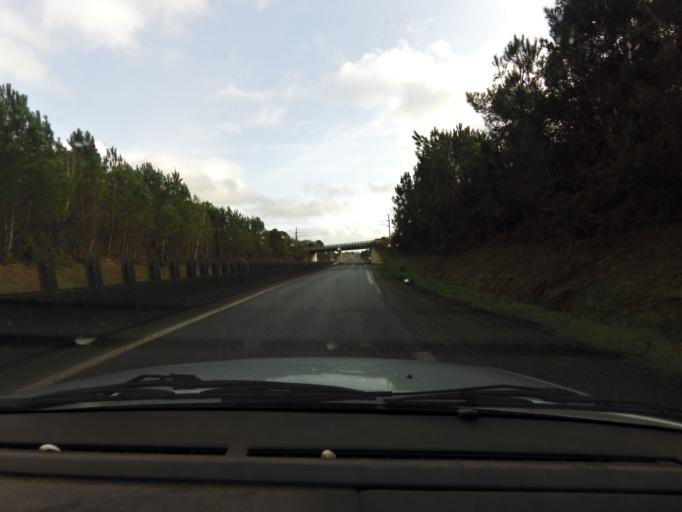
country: FR
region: Brittany
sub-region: Departement du Morbihan
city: Pluherlin
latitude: 47.6739
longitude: -2.3651
